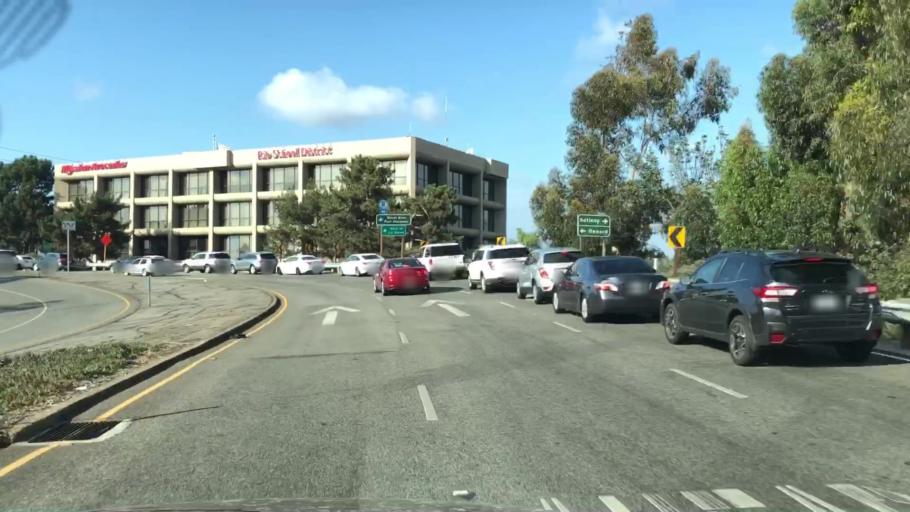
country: US
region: California
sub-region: Ventura County
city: El Rio
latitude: 34.2318
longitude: -119.1719
